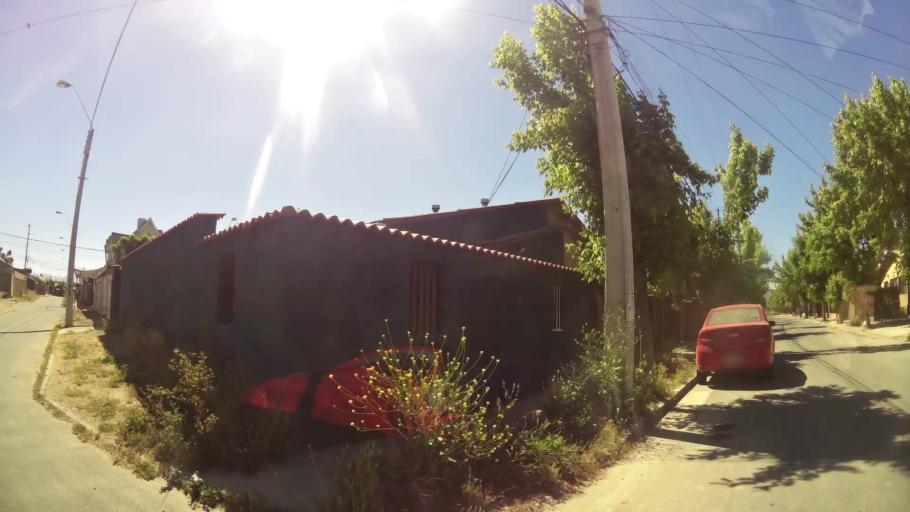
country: CL
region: Valparaiso
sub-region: Provincia de Marga Marga
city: Quilpue
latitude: -33.3087
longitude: -71.4151
